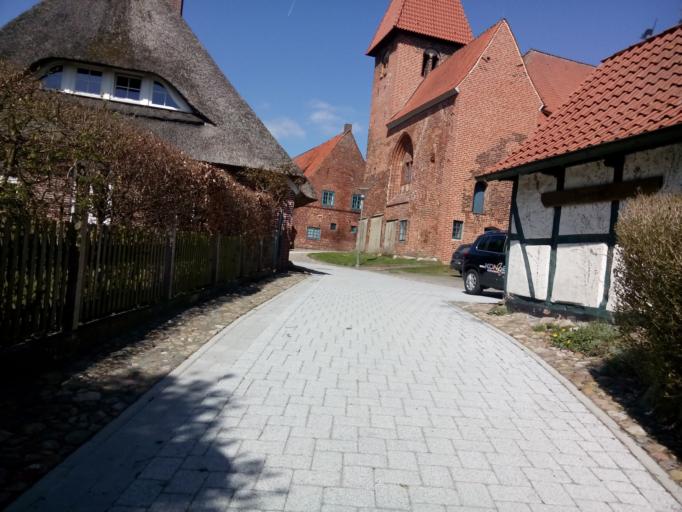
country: DE
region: Lower Saxony
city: Osterholz-Scharmbeck
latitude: 53.2241
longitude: 8.8119
